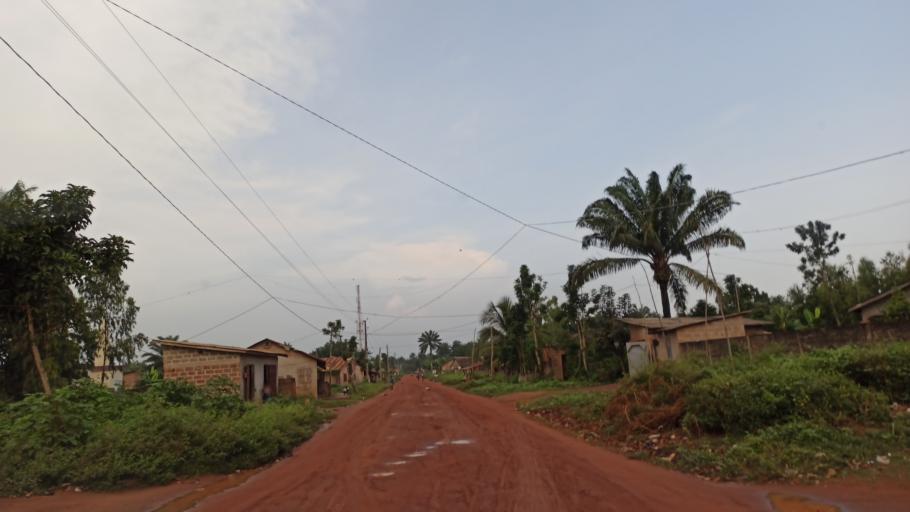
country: BJ
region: Queme
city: Porto-Novo
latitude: 6.4954
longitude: 2.6930
